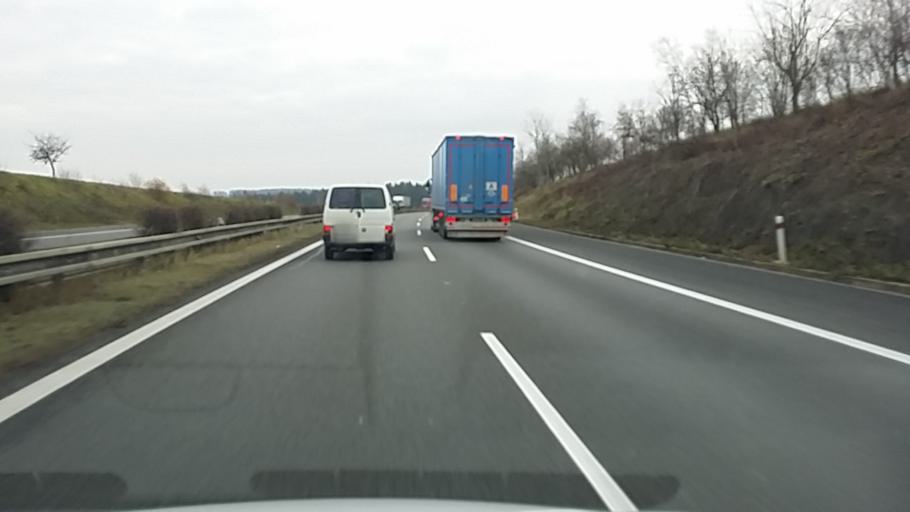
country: CZ
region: Central Bohemia
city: Zruc nad Sazavou
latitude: 49.7052
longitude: 15.0869
